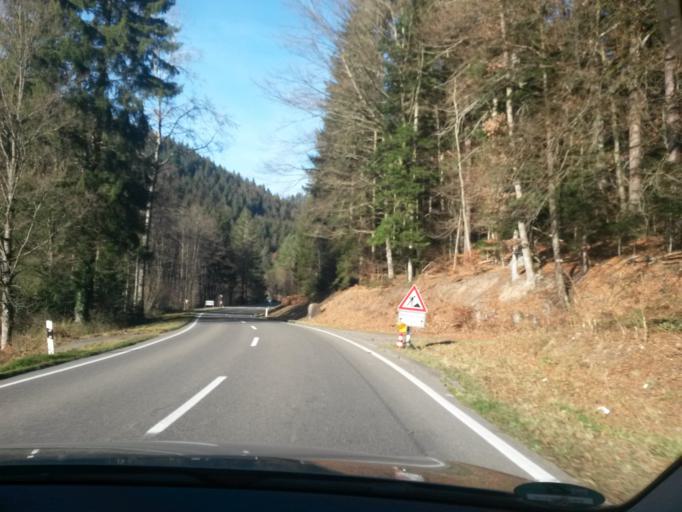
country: DE
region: Baden-Wuerttemberg
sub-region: Karlsruhe Region
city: Bad Wildbad
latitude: 48.7377
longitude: 8.5784
